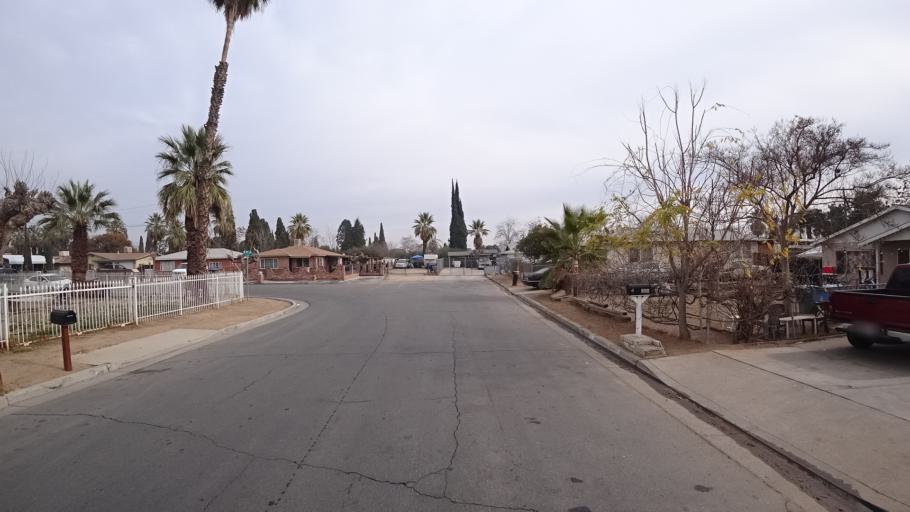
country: US
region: California
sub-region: Kern County
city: Bakersfield
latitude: 35.3616
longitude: -118.9994
